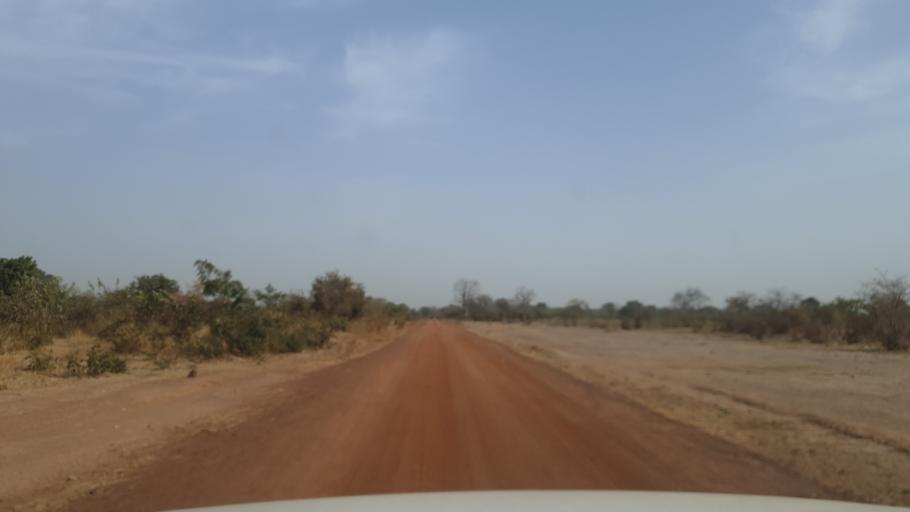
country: ML
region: Koulikoro
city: Kolokani
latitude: 13.3122
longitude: -8.2788
